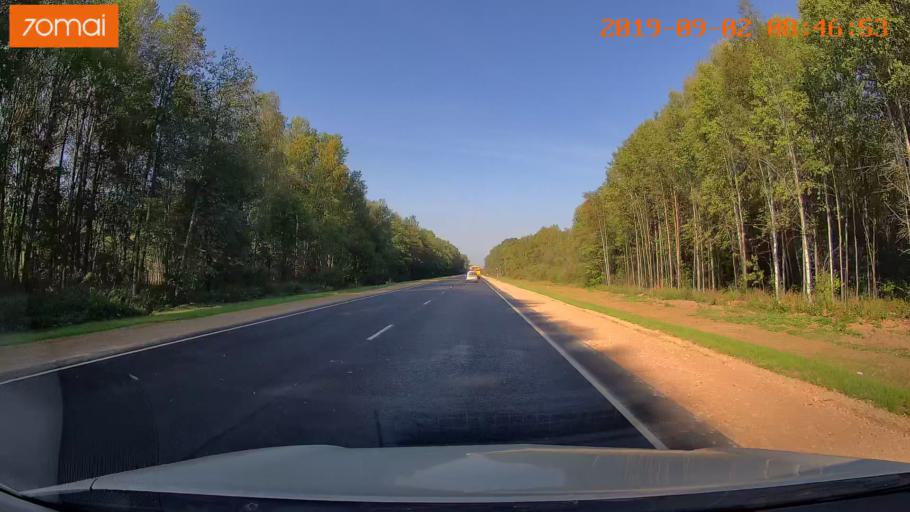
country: RU
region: Kaluga
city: Medyn'
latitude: 54.9683
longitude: 35.9672
